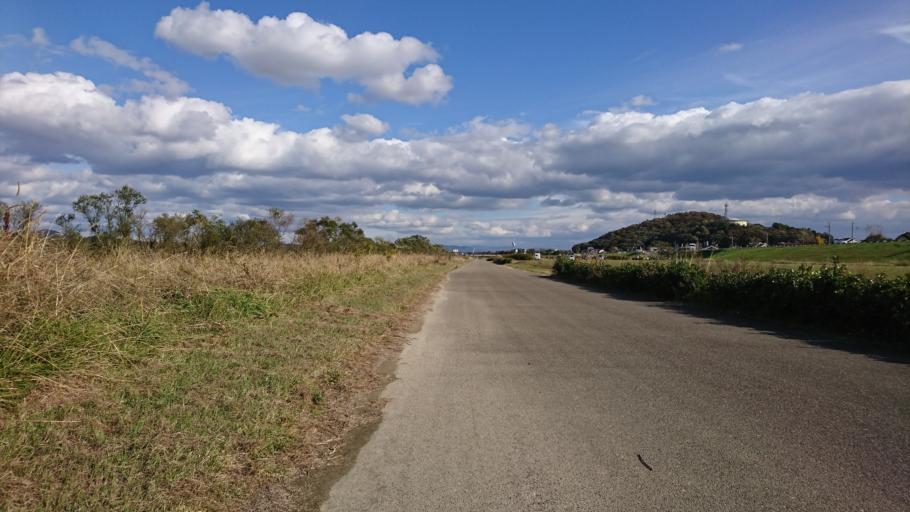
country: JP
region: Hyogo
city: Kakogawacho-honmachi
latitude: 34.7943
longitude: 134.8771
